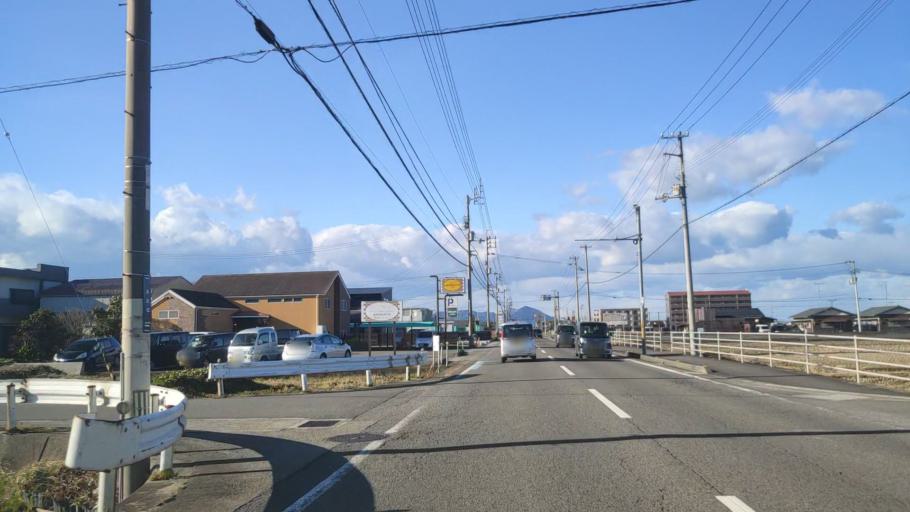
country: JP
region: Ehime
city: Saijo
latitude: 33.9119
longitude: 133.1095
